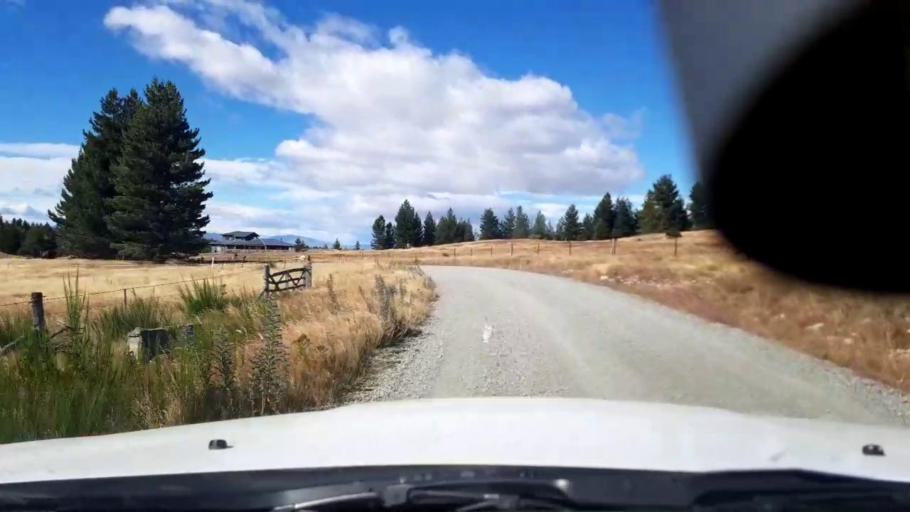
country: NZ
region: Canterbury
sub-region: Timaru District
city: Pleasant Point
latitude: -44.0102
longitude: 170.4724
